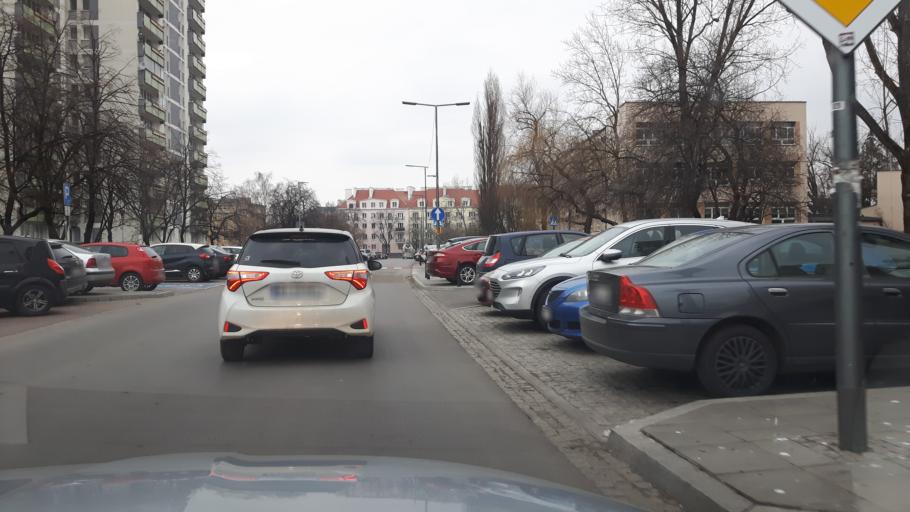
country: PL
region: Masovian Voivodeship
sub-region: Warszawa
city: Praga Poludnie
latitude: 52.2431
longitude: 21.0711
